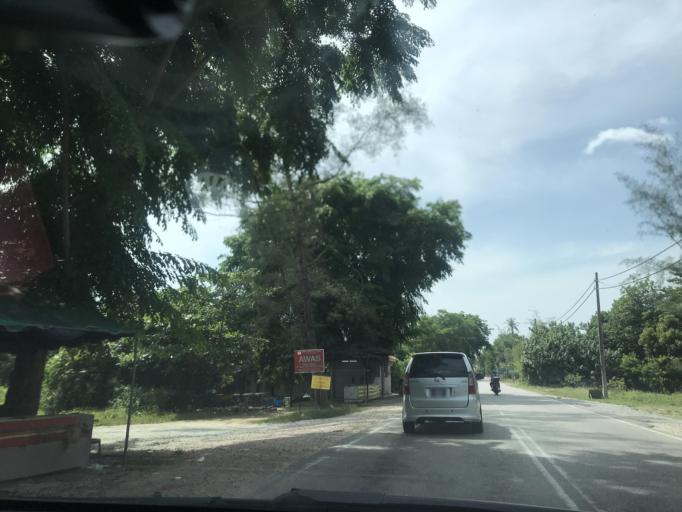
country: MY
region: Kelantan
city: Tumpat
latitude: 6.2064
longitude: 102.1455
